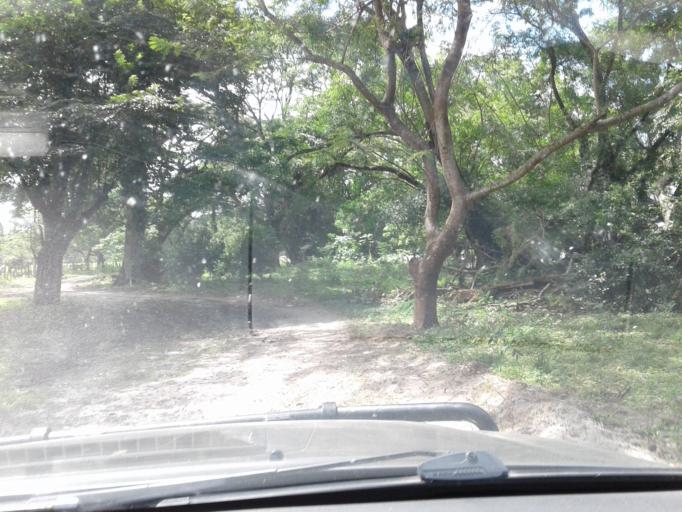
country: NI
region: Rivas
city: Cardenas
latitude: 11.1797
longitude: -85.4694
